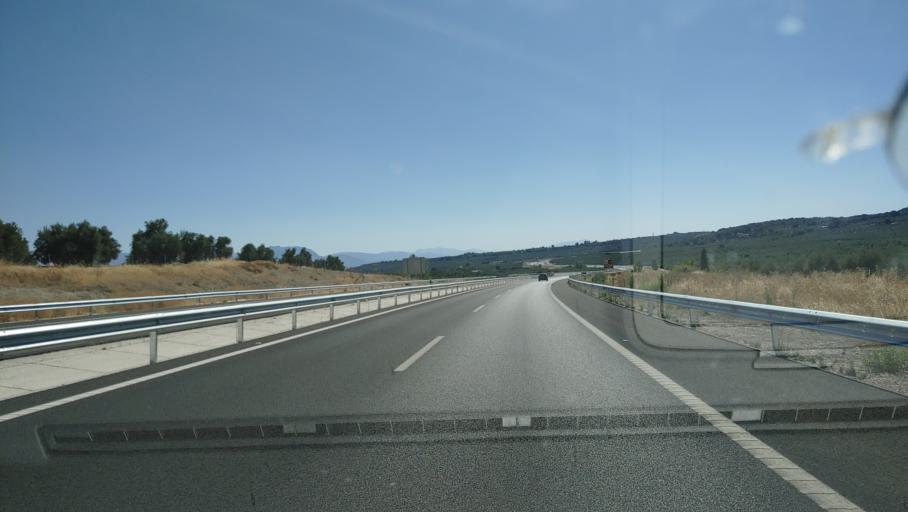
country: ES
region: Andalusia
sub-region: Provincia de Jaen
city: Torreperogil
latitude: 38.0451
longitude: -3.3121
